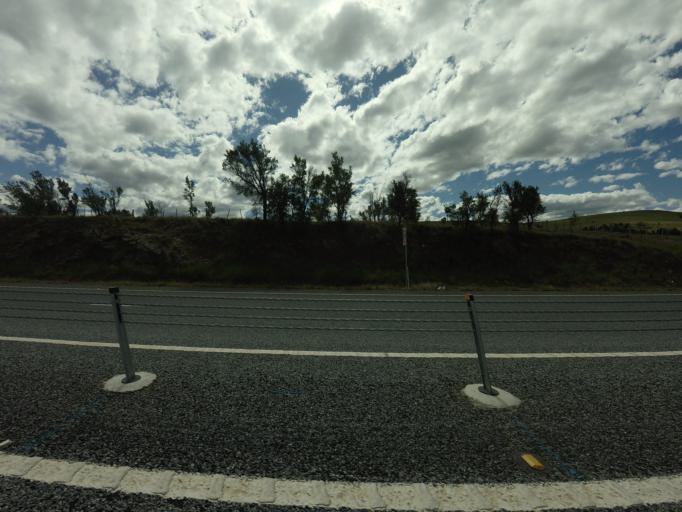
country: AU
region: Tasmania
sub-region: Northern Midlands
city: Evandale
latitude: -42.1263
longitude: 147.4327
